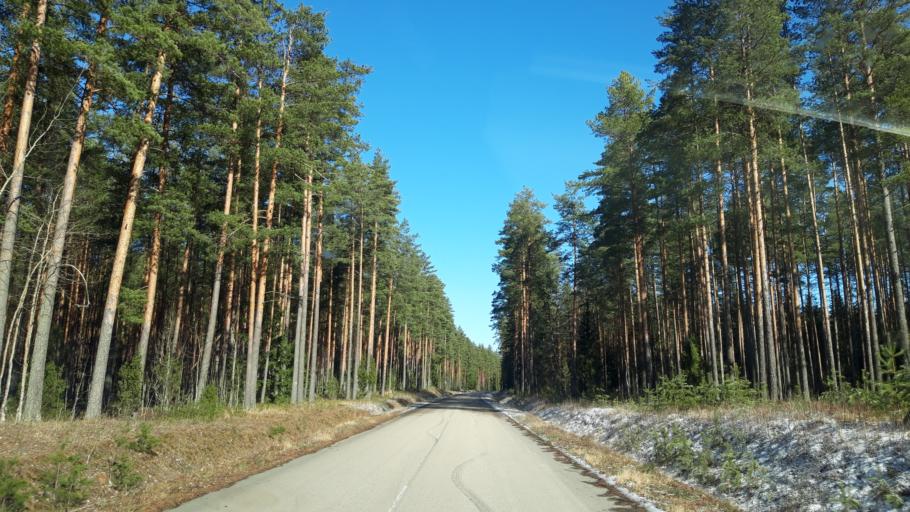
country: LV
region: Strenci
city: Strenci
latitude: 57.5801
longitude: 25.7131
